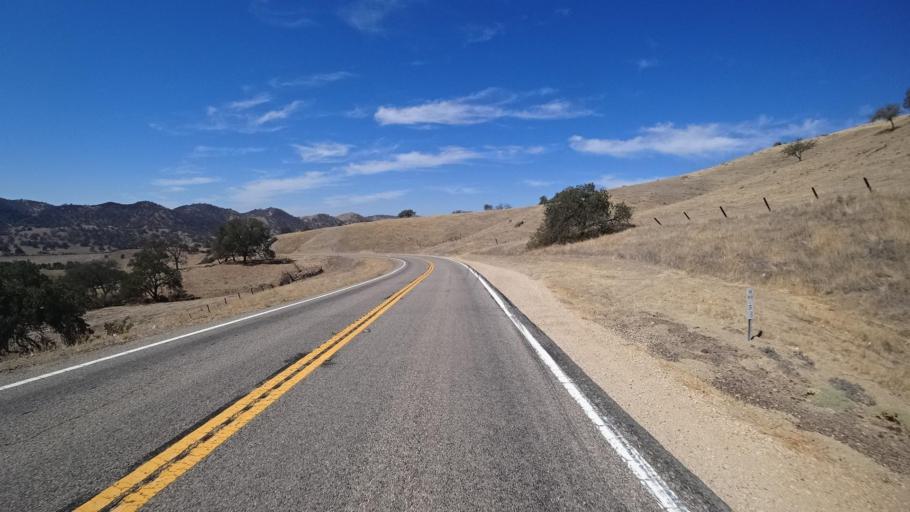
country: US
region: California
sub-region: Monterey County
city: King City
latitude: 36.1913
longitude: -120.8059
